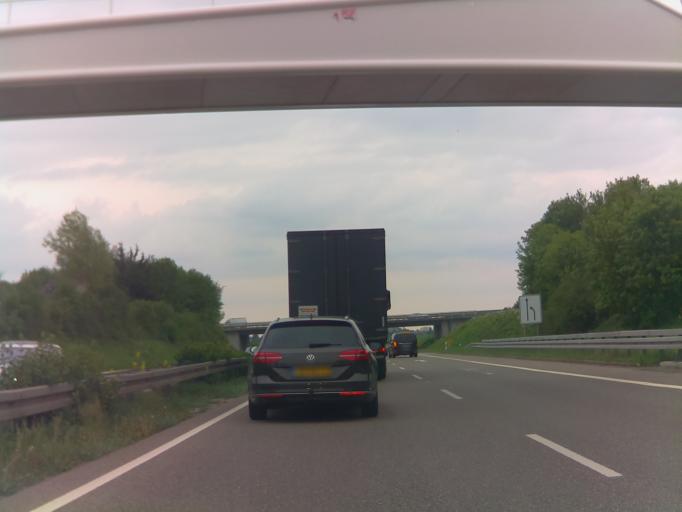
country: DE
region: Baden-Wuerttemberg
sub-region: Regierungsbezirk Stuttgart
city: Magstadt
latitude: 48.6989
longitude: 8.9664
